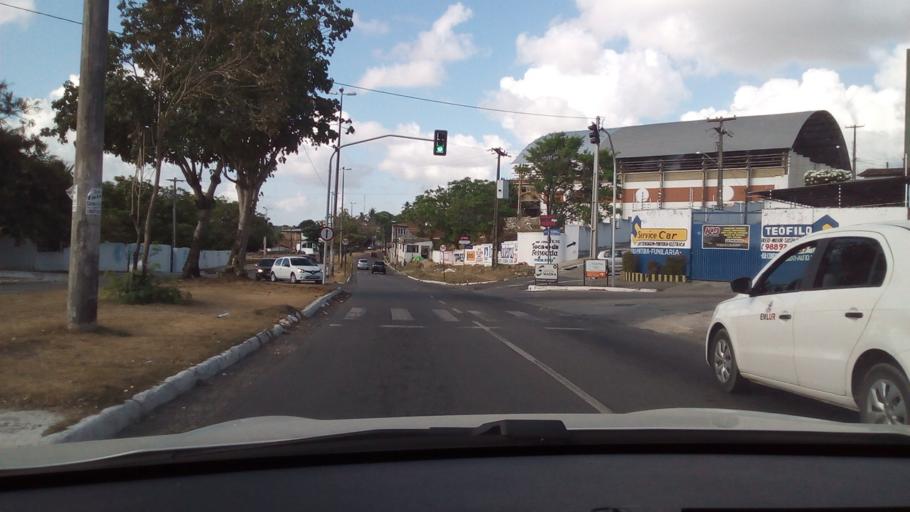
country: BR
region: Paraiba
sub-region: Joao Pessoa
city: Joao Pessoa
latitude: -7.1278
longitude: -34.8530
